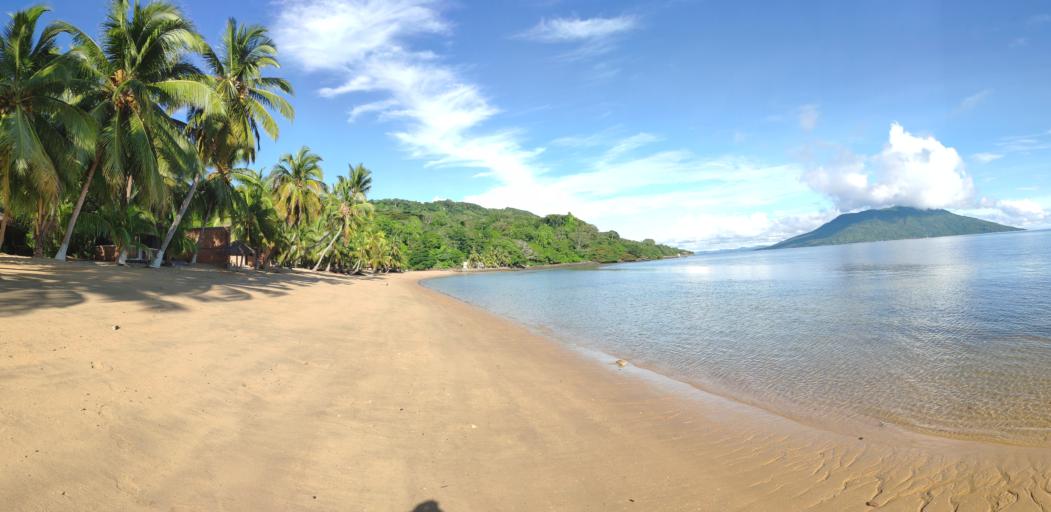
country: MG
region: Diana
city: Ambanja
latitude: -13.5479
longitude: 48.3648
